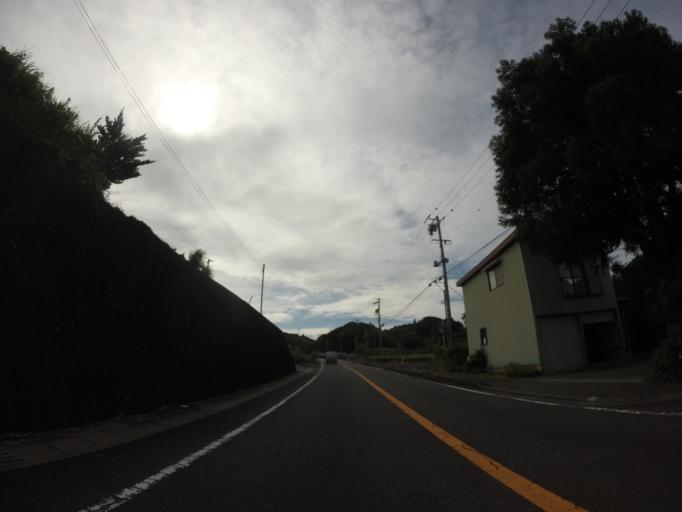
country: JP
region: Shizuoka
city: Shimada
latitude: 34.7856
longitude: 138.1547
